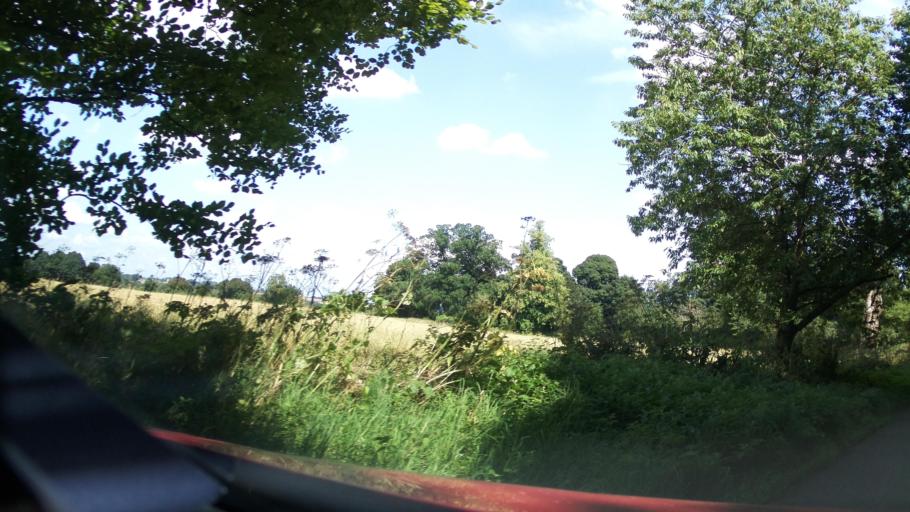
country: GB
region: England
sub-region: West Berkshire
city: Farnborough
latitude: 51.5106
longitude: -1.3933
